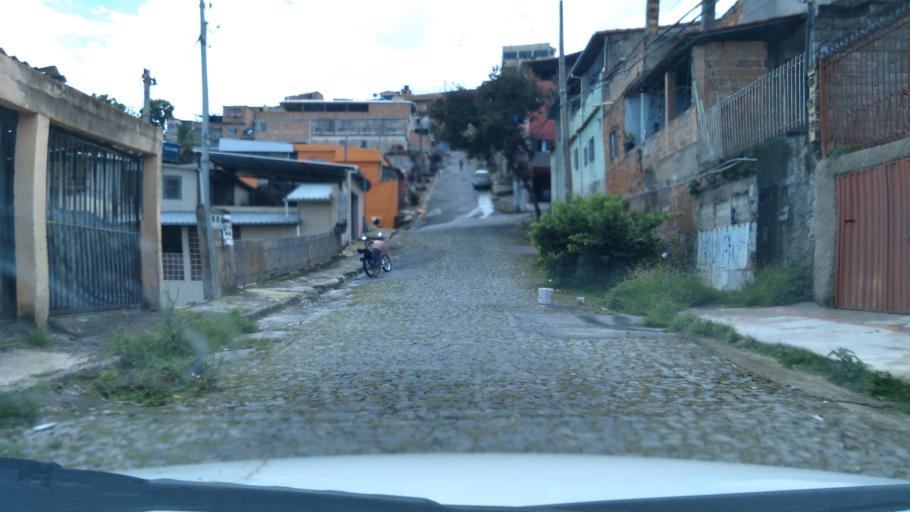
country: BR
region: Minas Gerais
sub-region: Belo Horizonte
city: Belo Horizonte
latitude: -19.8941
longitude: -43.8922
